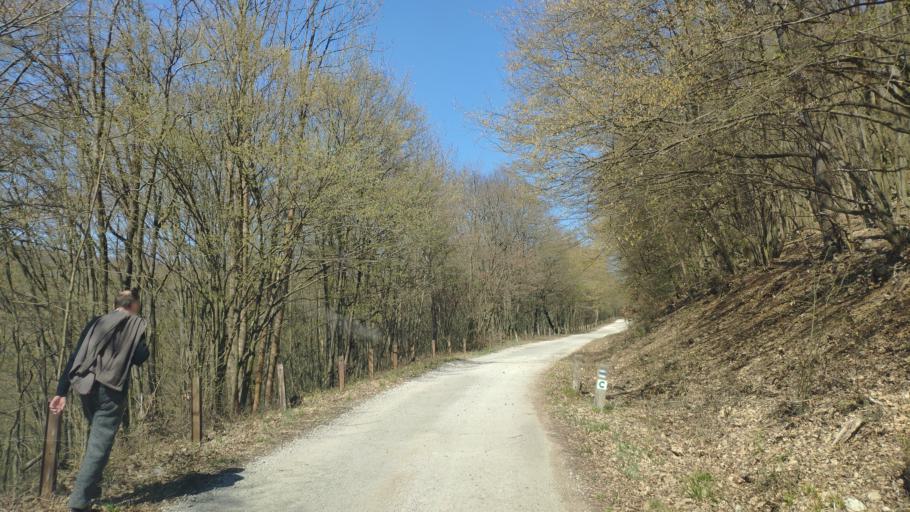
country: SK
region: Kosicky
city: Roznava
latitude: 48.5587
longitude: 20.4068
